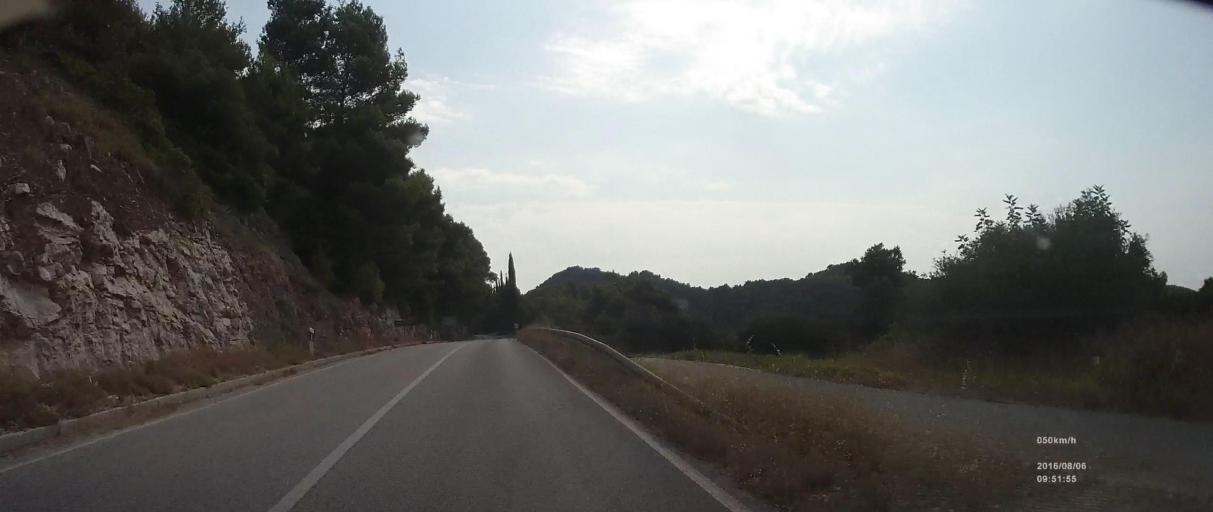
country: HR
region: Dubrovacko-Neretvanska
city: Blato
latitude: 42.7308
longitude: 17.5696
